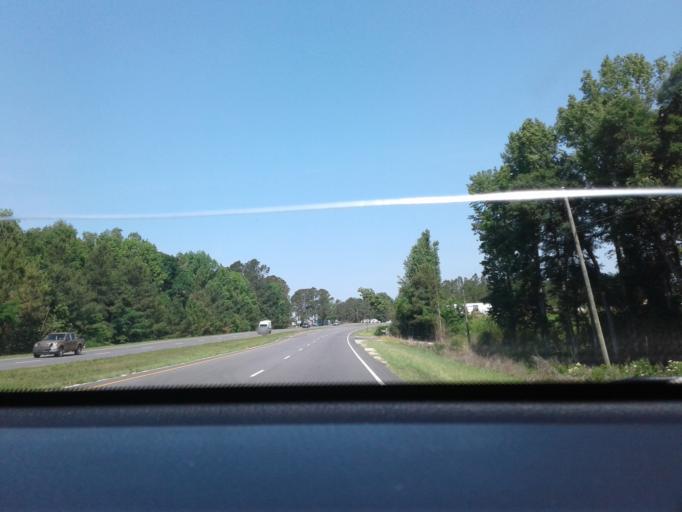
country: US
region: North Carolina
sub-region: Harnett County
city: Erwin
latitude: 35.3458
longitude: -78.6848
